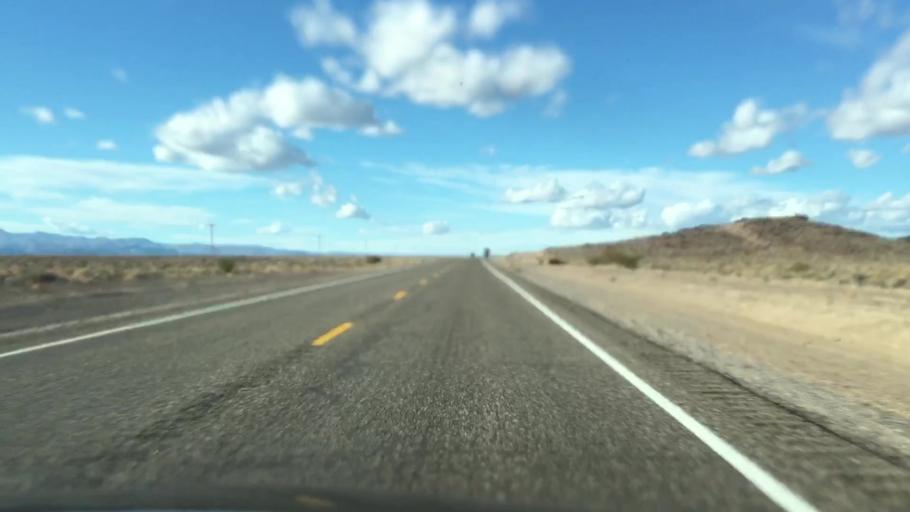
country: US
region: Nevada
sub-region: Nye County
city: Beatty
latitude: 37.1913
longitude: -116.9443
